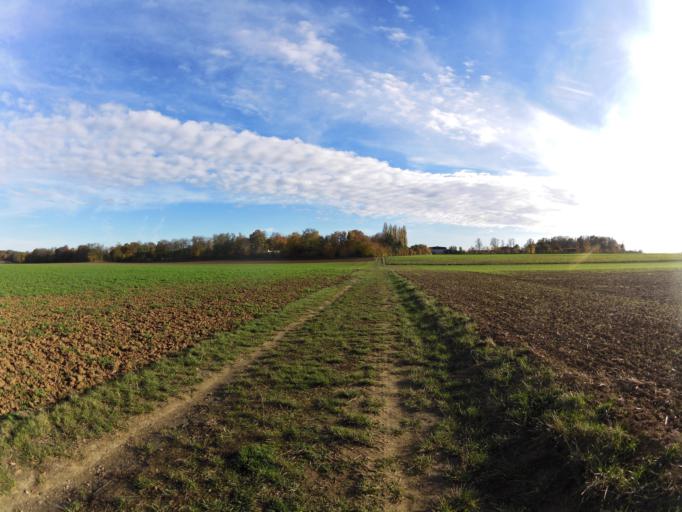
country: DE
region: Bavaria
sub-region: Regierungsbezirk Unterfranken
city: Giebelstadt
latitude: 49.6589
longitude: 9.9658
